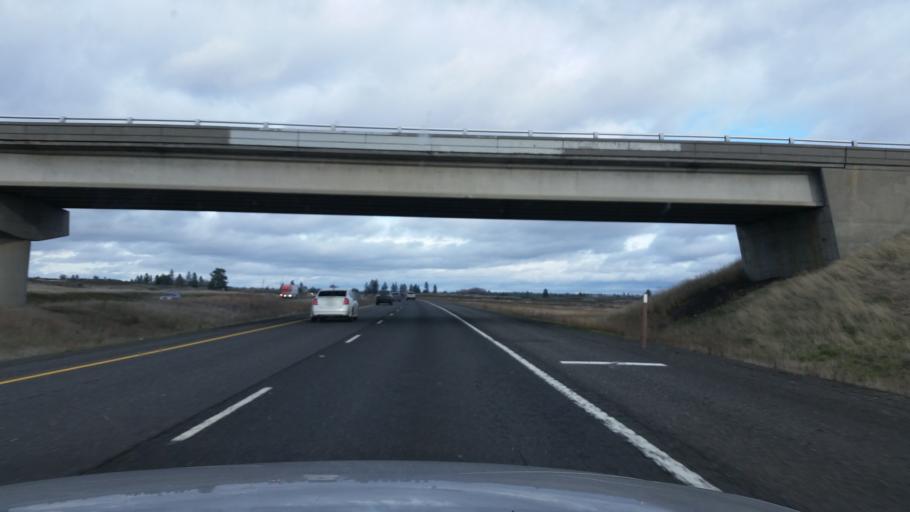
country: US
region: Washington
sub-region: Spokane County
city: Medical Lake
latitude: 47.3953
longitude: -117.8407
